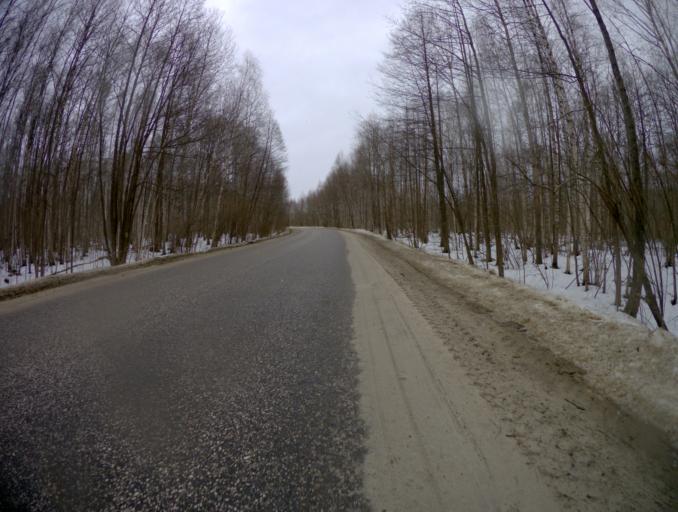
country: RU
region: Vladimir
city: Orgtrud
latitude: 56.1520
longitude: 40.5795
